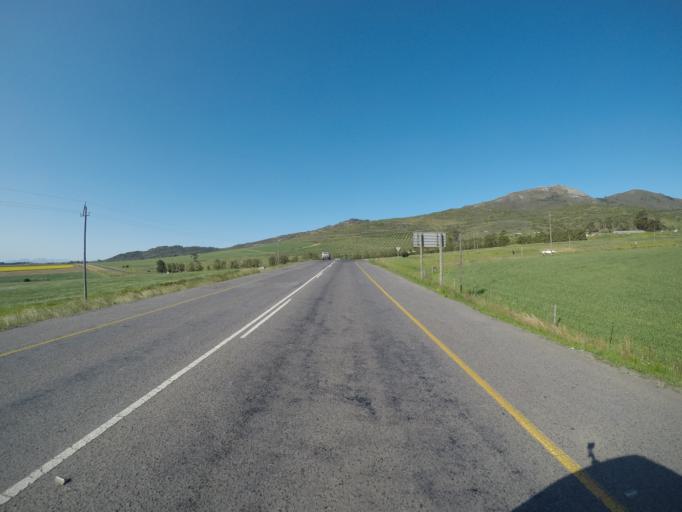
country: ZA
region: Western Cape
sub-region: Cape Winelands District Municipality
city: Noorder-Paarl
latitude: -33.7076
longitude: 18.8918
